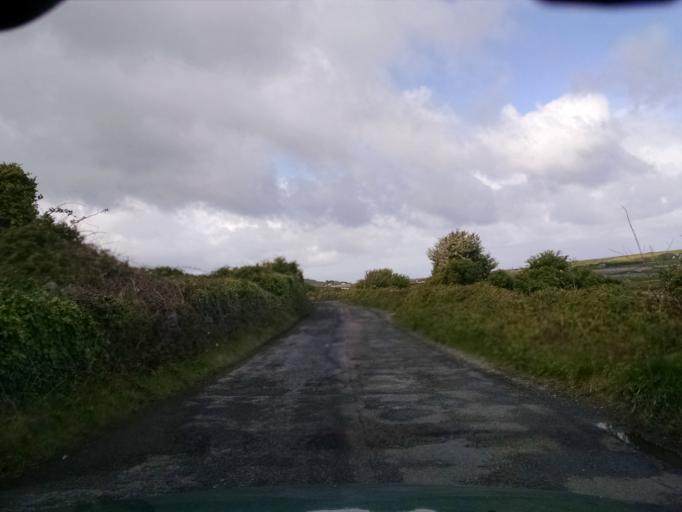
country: IE
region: Connaught
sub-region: County Galway
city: Gaillimh
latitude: 53.1561
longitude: -9.0611
